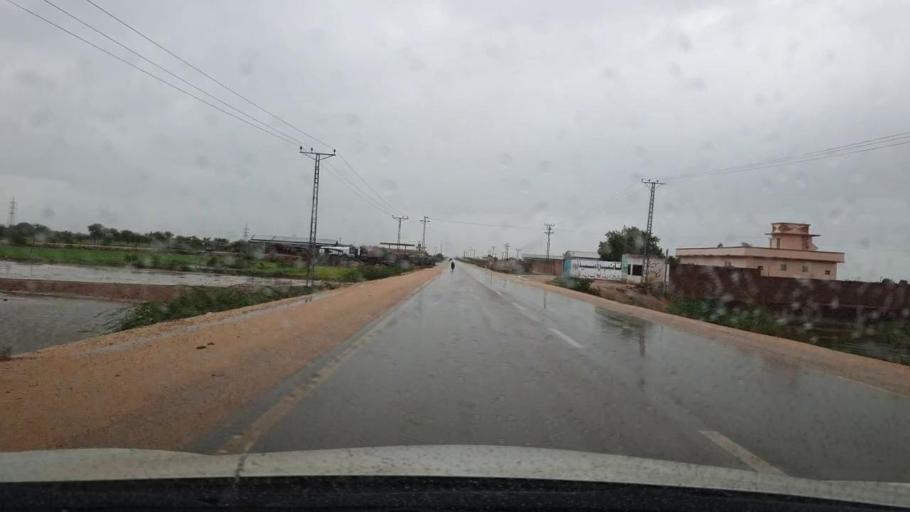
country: PK
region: Sindh
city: Kario
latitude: 24.6536
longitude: 68.5552
